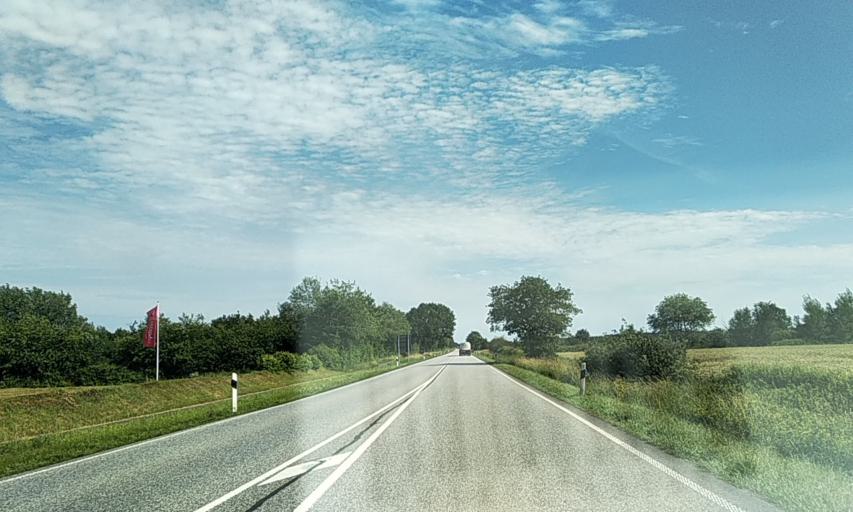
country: DE
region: Schleswig-Holstein
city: Kropp
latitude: 54.4195
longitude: 9.5301
